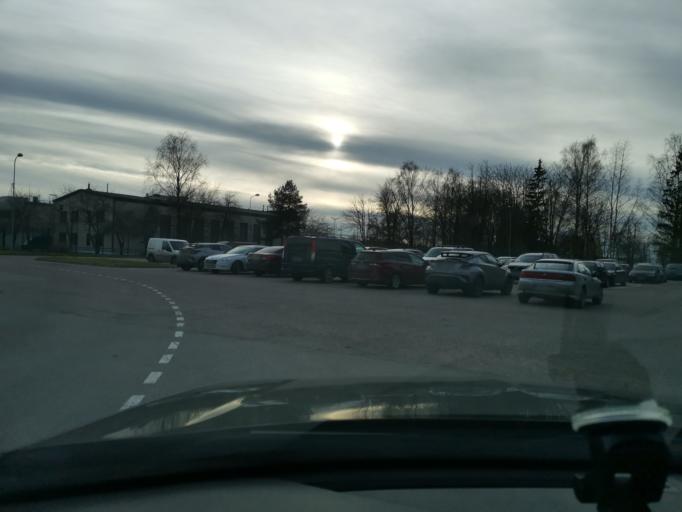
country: EE
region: Ida-Virumaa
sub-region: Sillamaee linn
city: Sillamae
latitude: 59.2740
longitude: 27.9111
